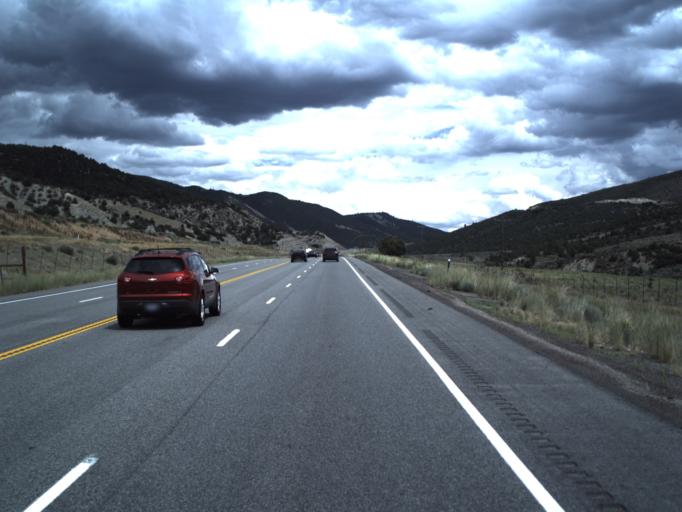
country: US
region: Utah
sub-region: Sanpete County
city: Fairview
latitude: 39.9295
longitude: -111.1785
